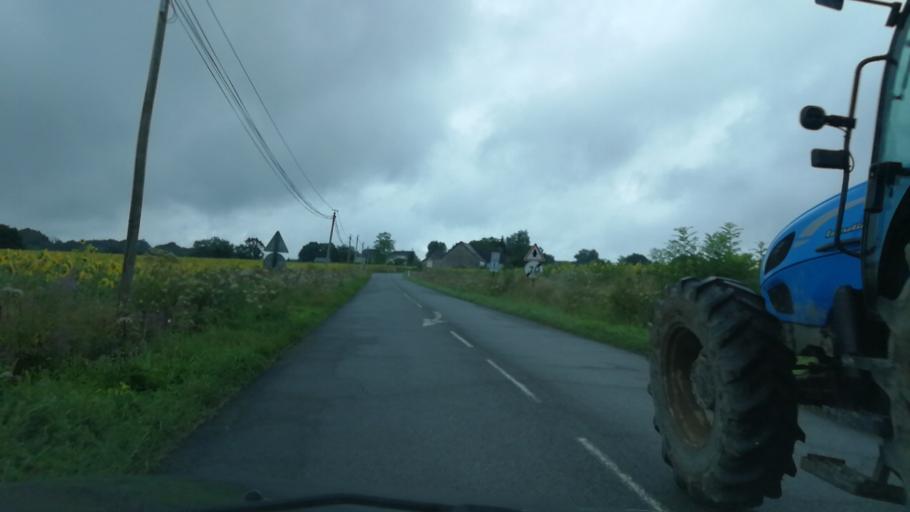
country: FR
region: Aquitaine
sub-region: Departement des Pyrenees-Atlantiques
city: Lucq-de-Bearn
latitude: 43.2963
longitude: -0.6651
